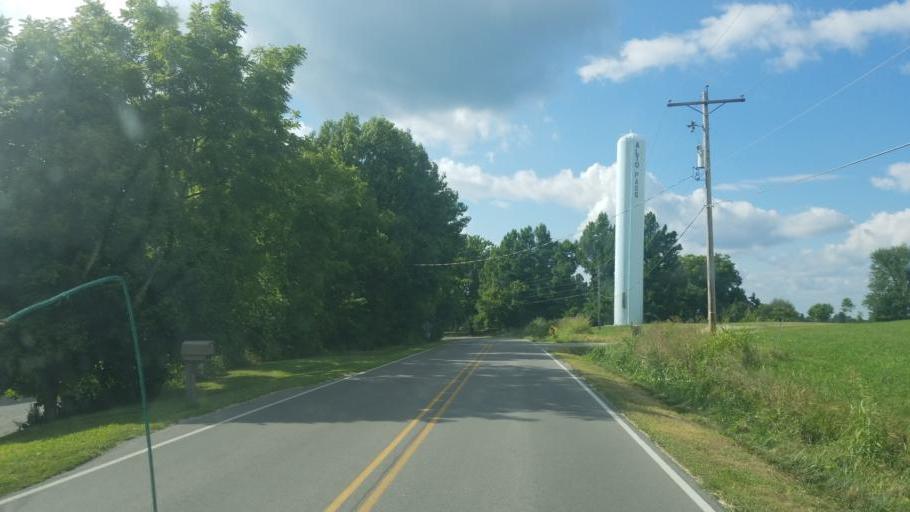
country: US
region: Illinois
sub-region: Union County
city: Cobden
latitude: 37.5605
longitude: -89.3055
